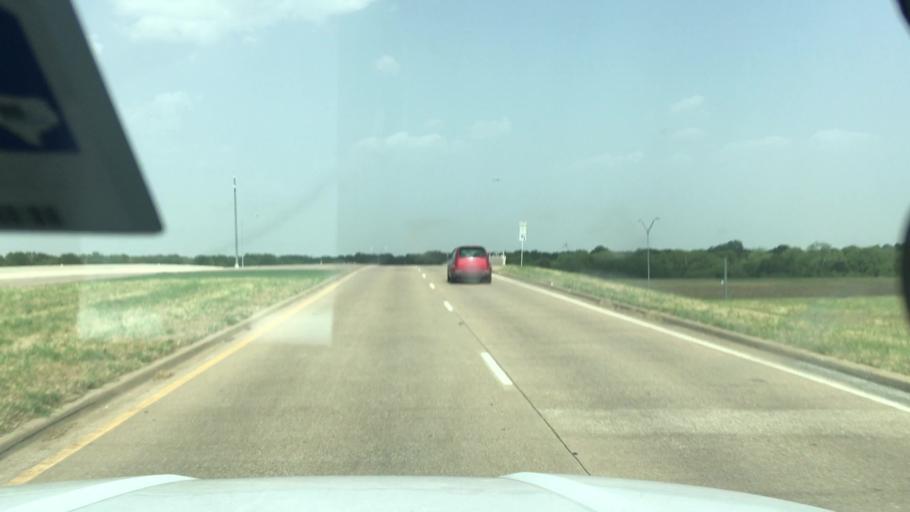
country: US
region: Texas
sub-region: Tarrant County
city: Euless
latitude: 32.8671
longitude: -97.0667
